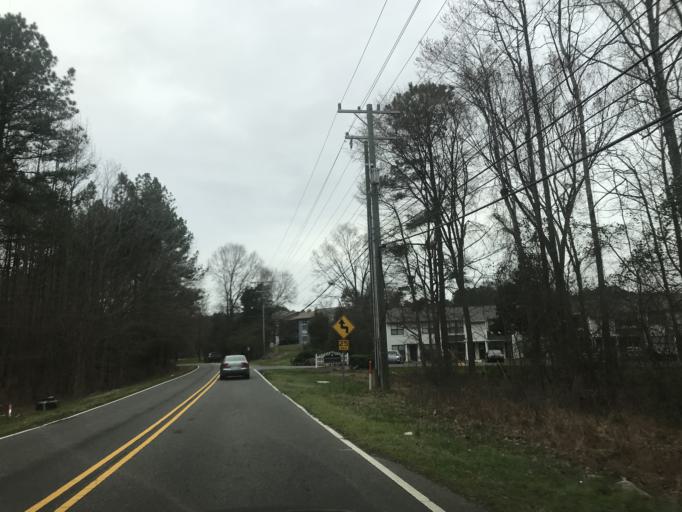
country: US
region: North Carolina
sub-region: Wake County
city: Morrisville
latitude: 35.8898
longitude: -78.8848
